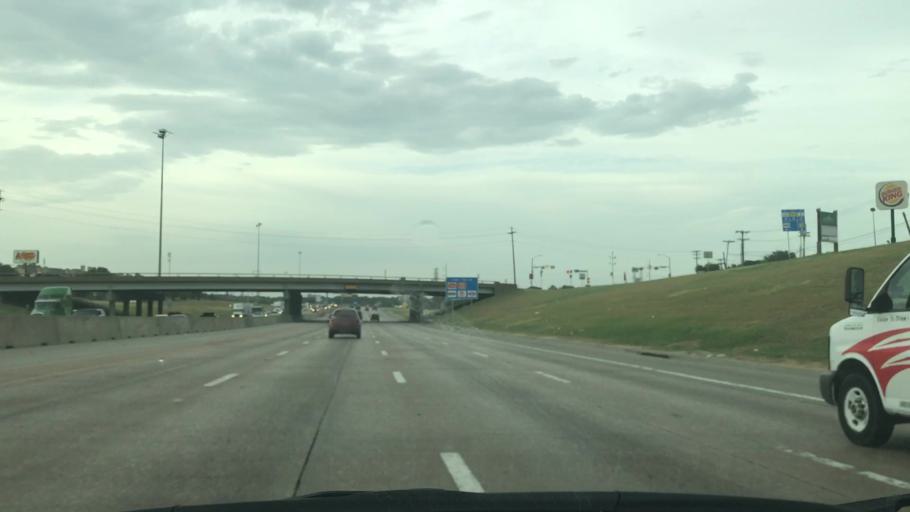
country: US
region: Texas
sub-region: Dallas County
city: Mesquite
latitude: 32.8339
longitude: -96.6319
